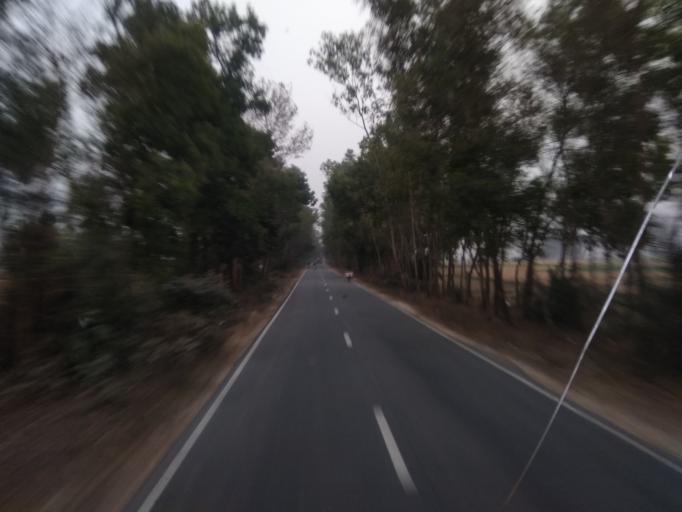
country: BD
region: Rajshahi
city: Bogra
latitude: 24.6578
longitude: 89.2650
